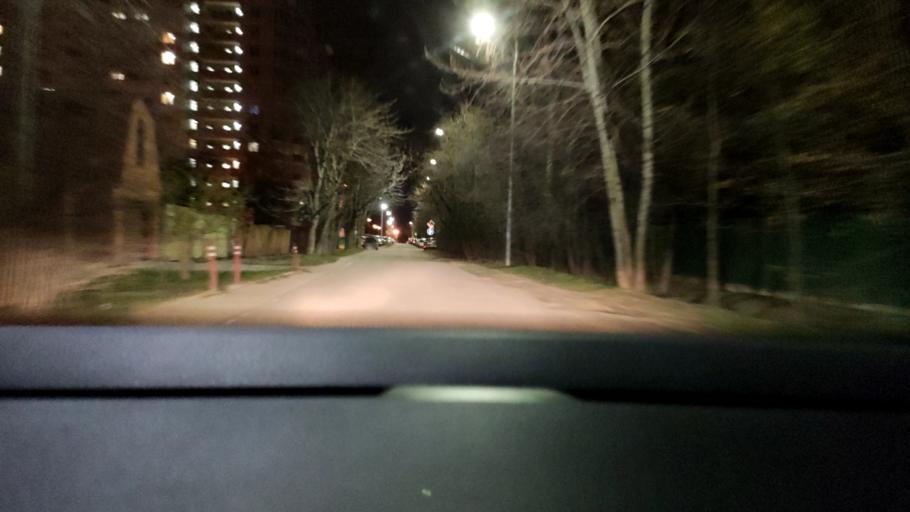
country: RU
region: Moskovskaya
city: Reutov
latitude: 55.7726
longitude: 37.8905
